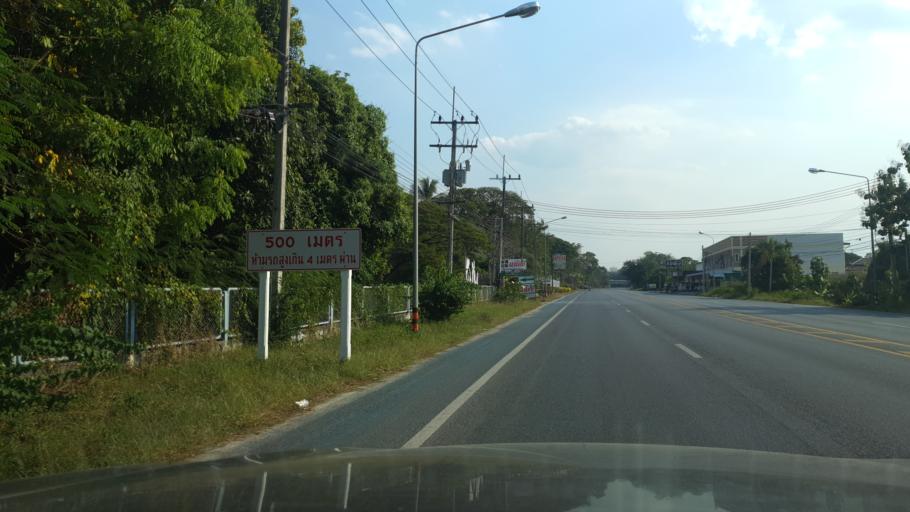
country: TH
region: Tak
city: Tak
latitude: 16.8624
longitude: 99.1209
